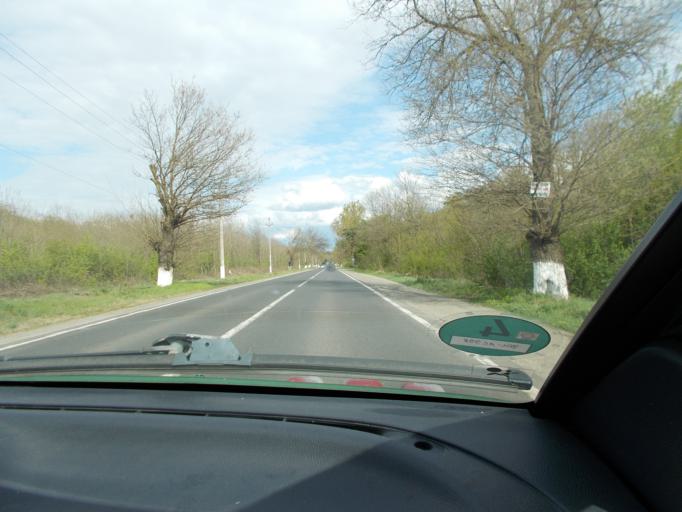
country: RO
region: Ilfov
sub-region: Comuna Ganeasa
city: Ganeasa
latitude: 44.4561
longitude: 26.2854
